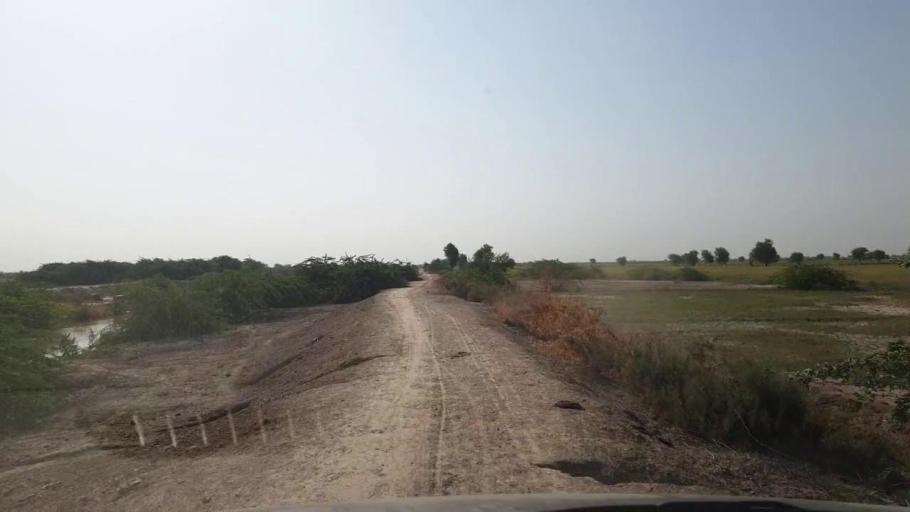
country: PK
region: Sindh
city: Kadhan
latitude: 24.5733
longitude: 69.0819
